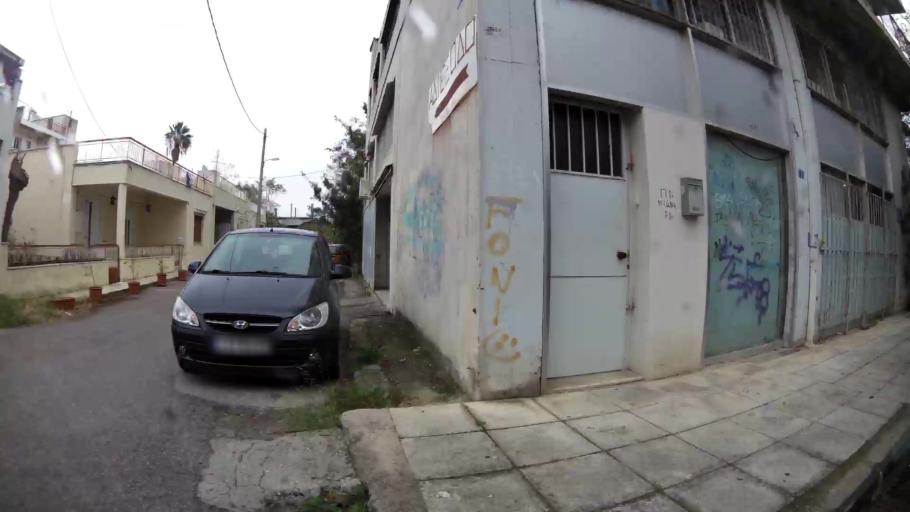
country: GR
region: Attica
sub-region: Nomarchia Athinas
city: Agioi Anargyroi
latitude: 38.0179
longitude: 23.7170
